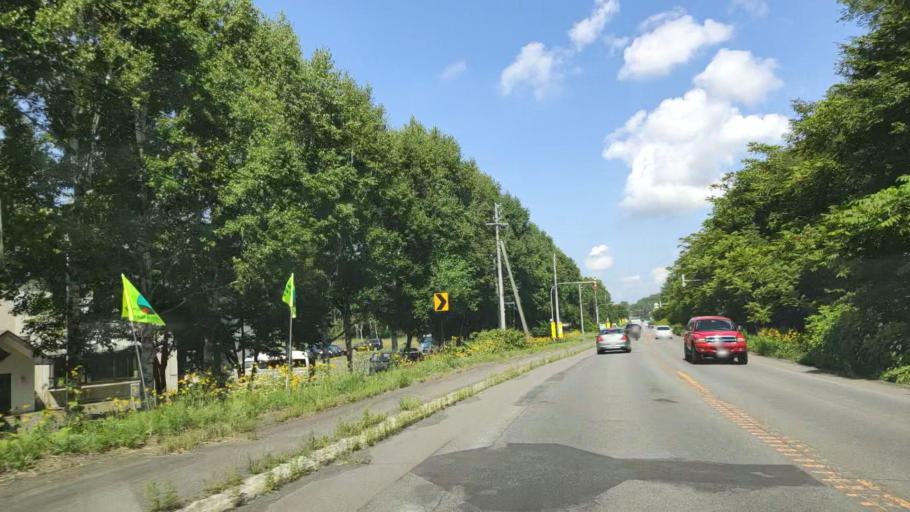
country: JP
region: Hokkaido
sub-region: Asahikawa-shi
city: Asahikawa
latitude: 43.6213
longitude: 142.4693
